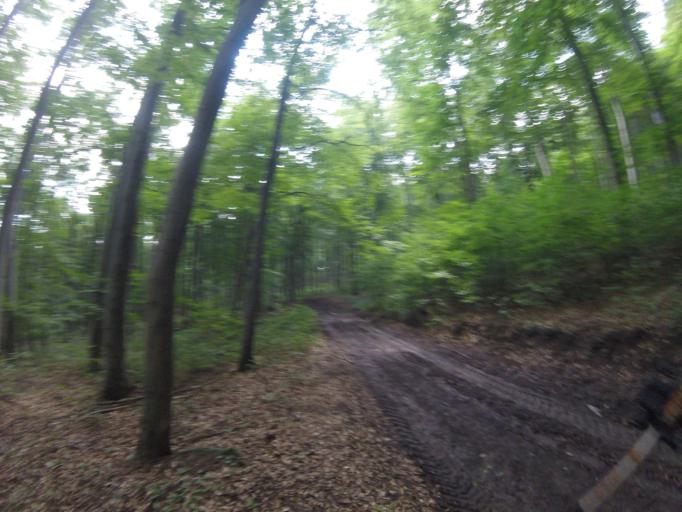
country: SK
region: Nitriansky
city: Sahy
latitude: 47.9587
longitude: 18.8810
